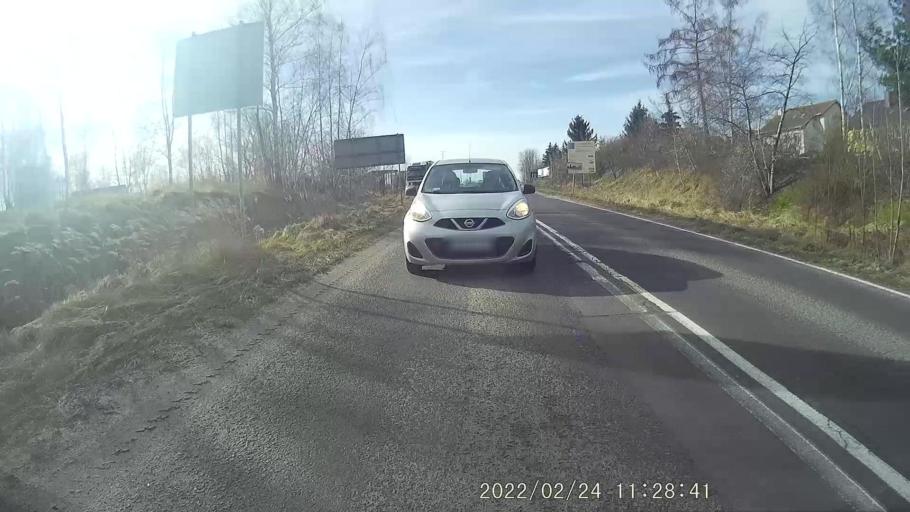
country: PL
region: Lower Silesian Voivodeship
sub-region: Powiat polkowicki
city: Przemkow
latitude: 51.5310
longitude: 15.6896
